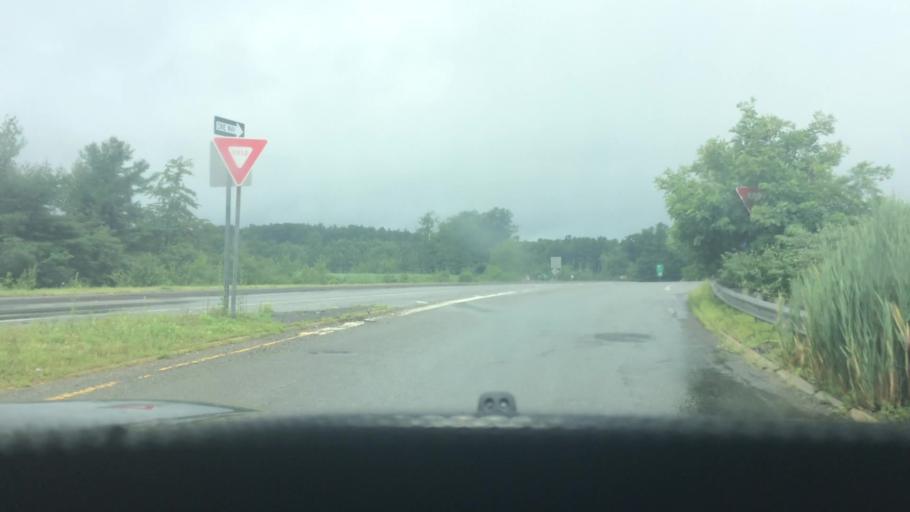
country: US
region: Massachusetts
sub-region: Worcester County
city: Westminster
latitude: 42.5596
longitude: -71.9324
